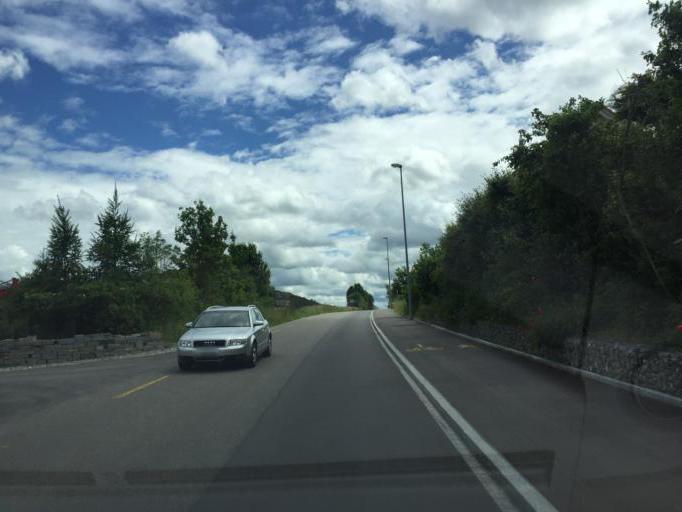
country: CH
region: Thurgau
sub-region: Frauenfeld District
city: Diessenhofen
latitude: 47.6823
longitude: 8.7585
